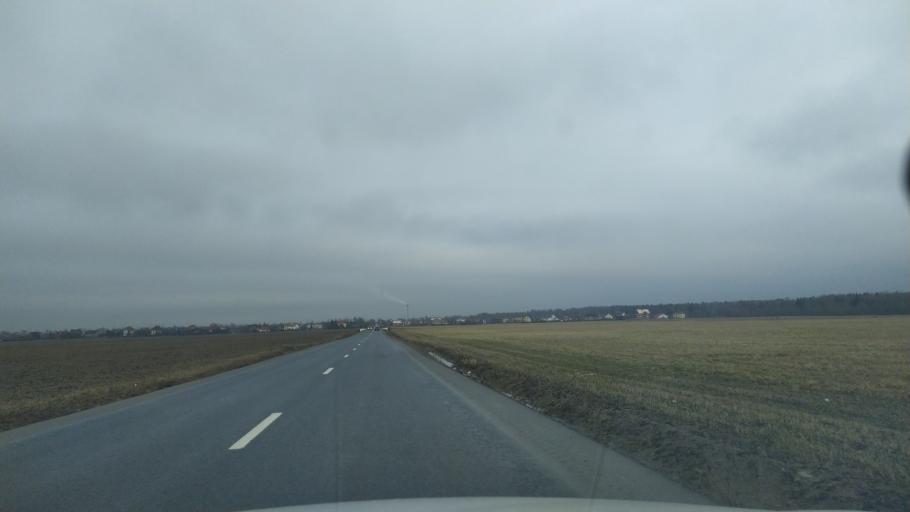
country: RU
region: St.-Petersburg
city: Aleksandrovskaya
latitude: 59.7160
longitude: 30.3370
